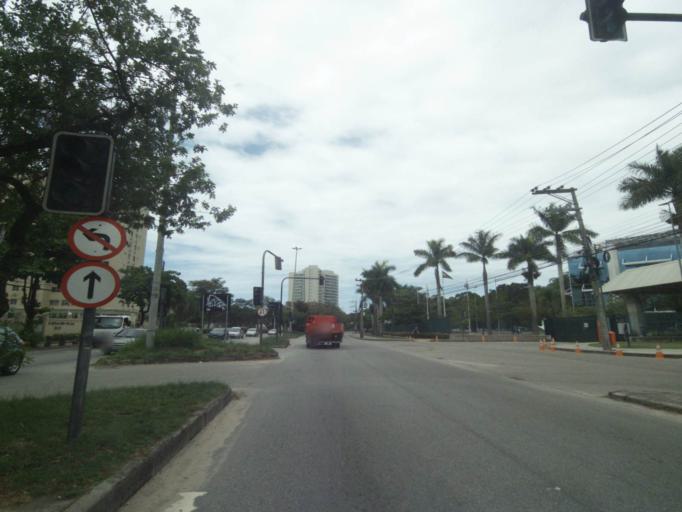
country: BR
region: Rio de Janeiro
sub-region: Nilopolis
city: Nilopolis
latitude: -22.9725
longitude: -43.4141
